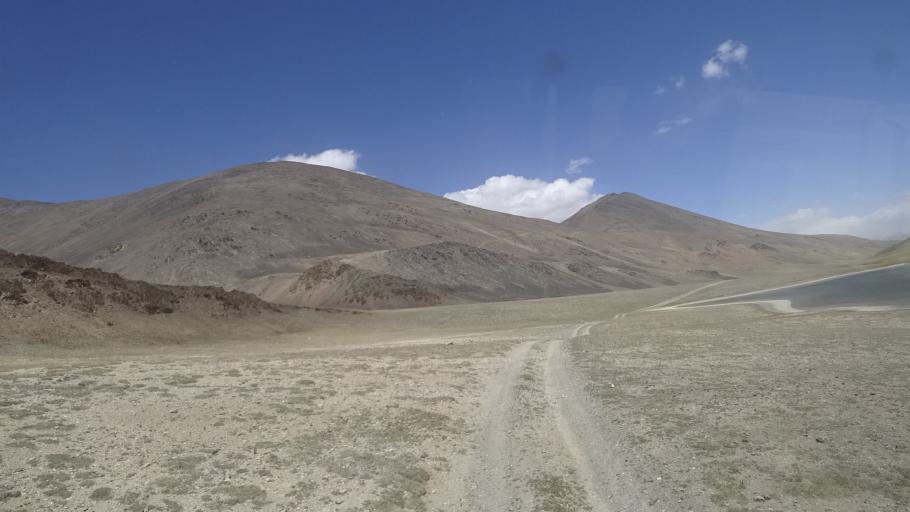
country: TJ
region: Gorno-Badakhshan
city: Murghob
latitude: 37.5208
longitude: 74.0609
